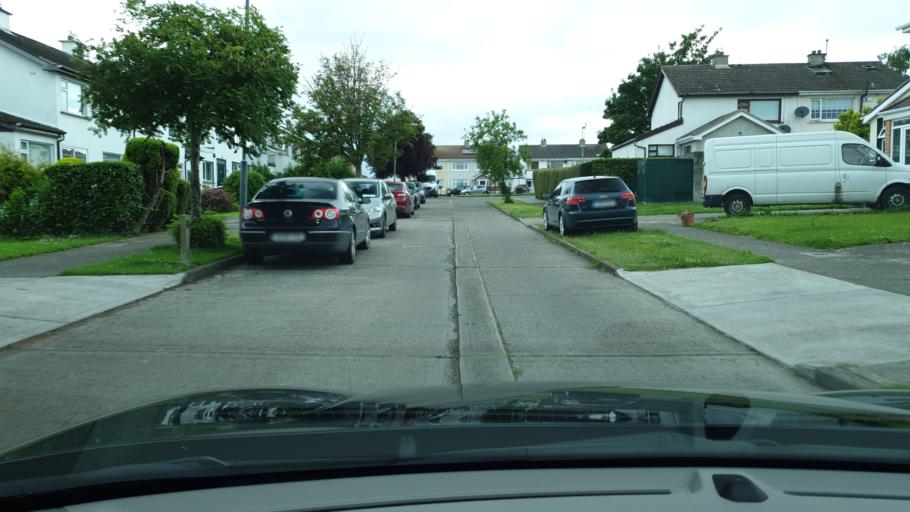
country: IE
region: Leinster
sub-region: An Mhi
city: Ashbourne
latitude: 53.5044
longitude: -6.4040
